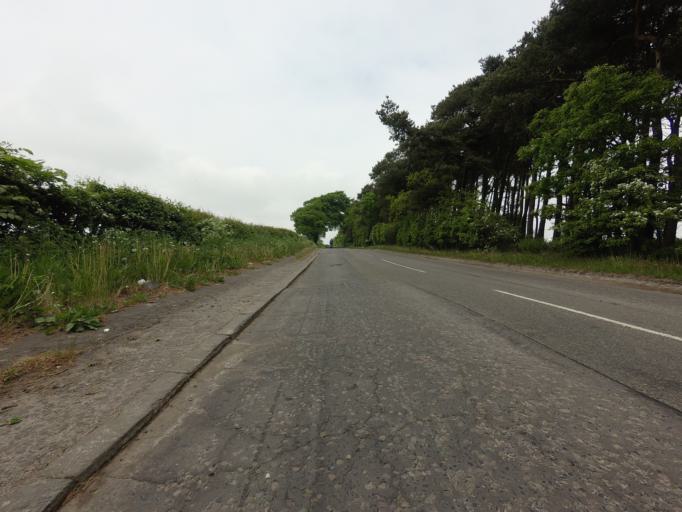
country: GB
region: Scotland
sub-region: Fife
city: Townhill
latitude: 56.0957
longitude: -3.4430
